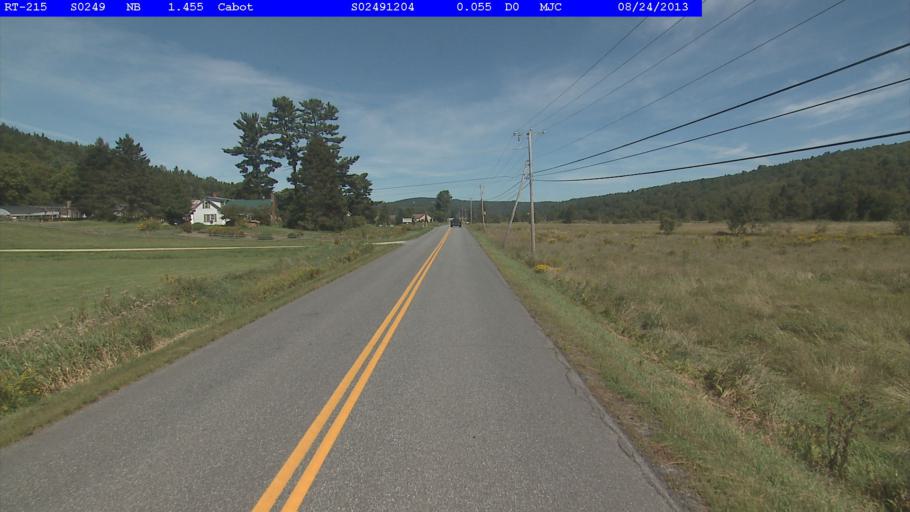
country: US
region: Vermont
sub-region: Caledonia County
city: Hardwick
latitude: 44.3683
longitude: -72.3371
